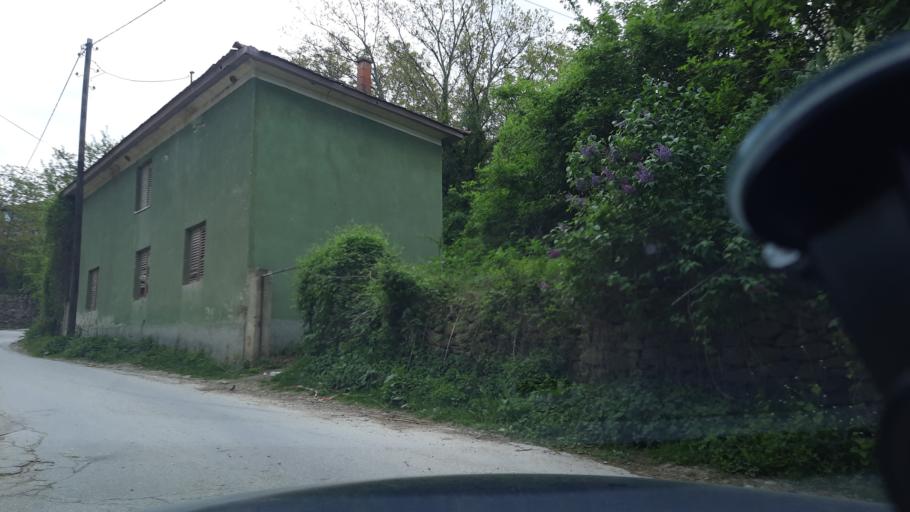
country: MK
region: Bitola
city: Bitola
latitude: 41.0241
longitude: 21.2845
